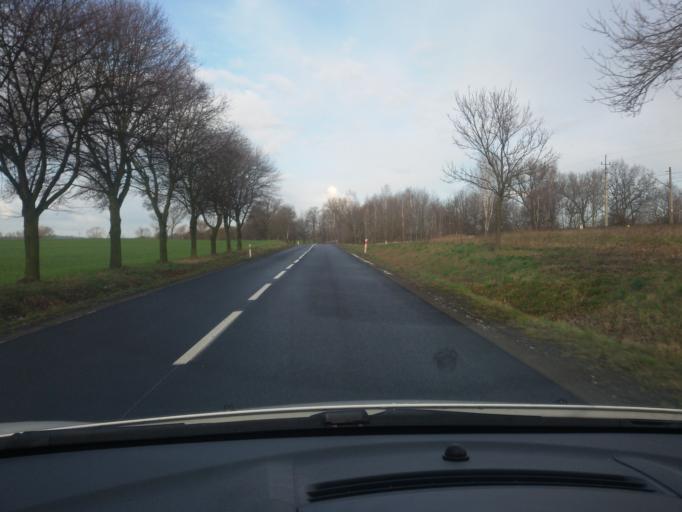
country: PL
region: Lower Silesian Voivodeship
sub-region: Powiat polkowicki
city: Gaworzyce
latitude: 51.6886
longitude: 15.9363
